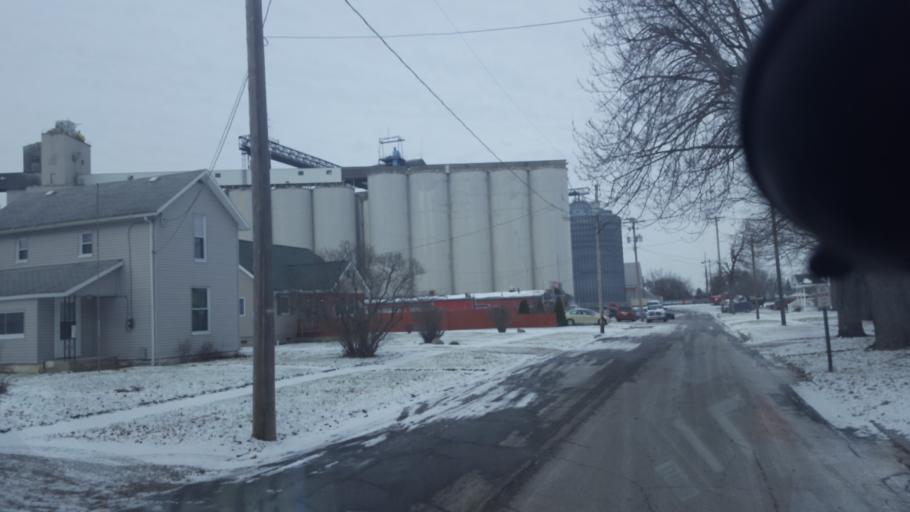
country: US
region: Ohio
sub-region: Marion County
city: Marion
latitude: 40.5925
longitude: -83.1093
